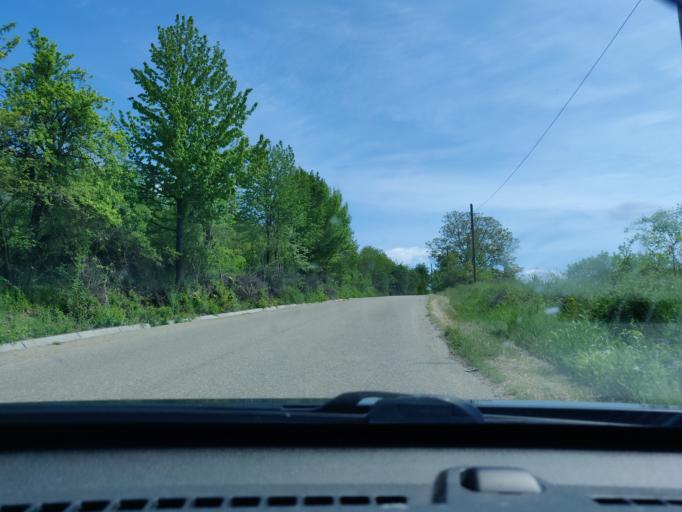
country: RO
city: Vizantea-Manastireasca
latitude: 45.9936
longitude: 26.7767
